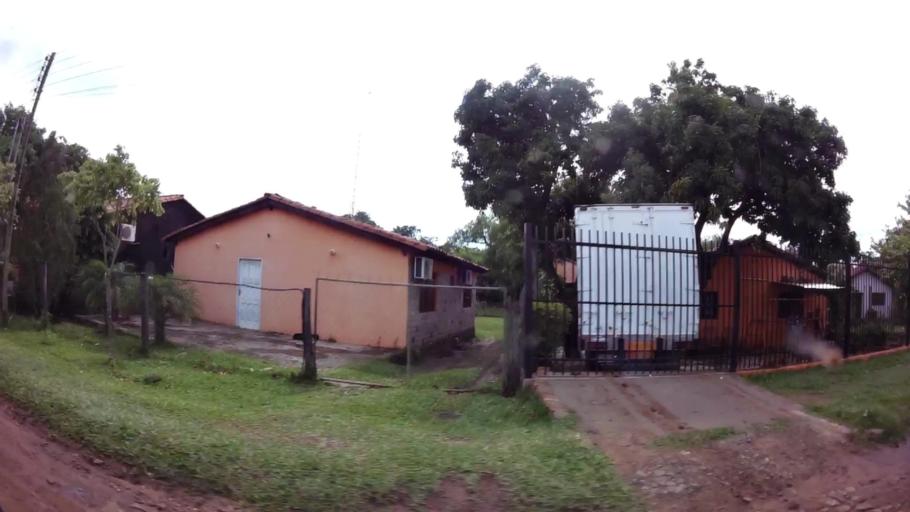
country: PY
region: Central
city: Limpio
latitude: -25.1282
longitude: -57.4749
